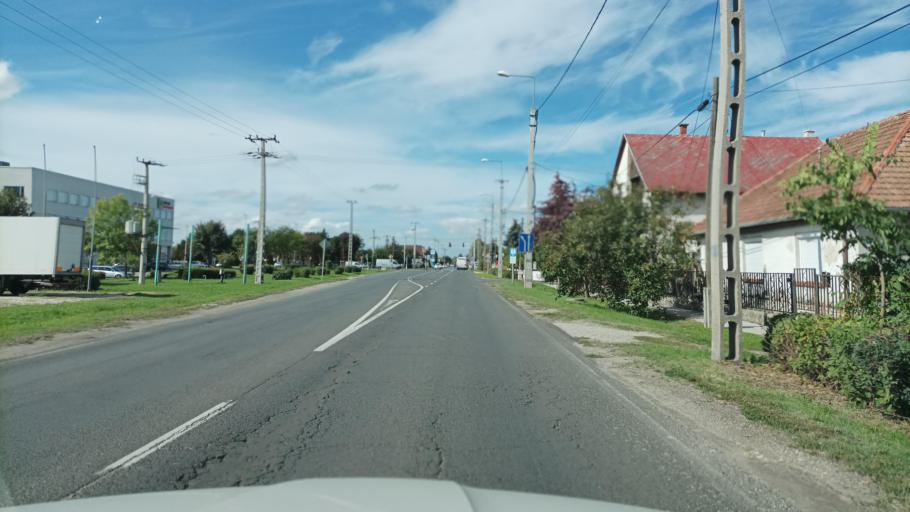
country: HU
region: Pest
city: Ullo
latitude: 47.3798
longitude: 19.3561
